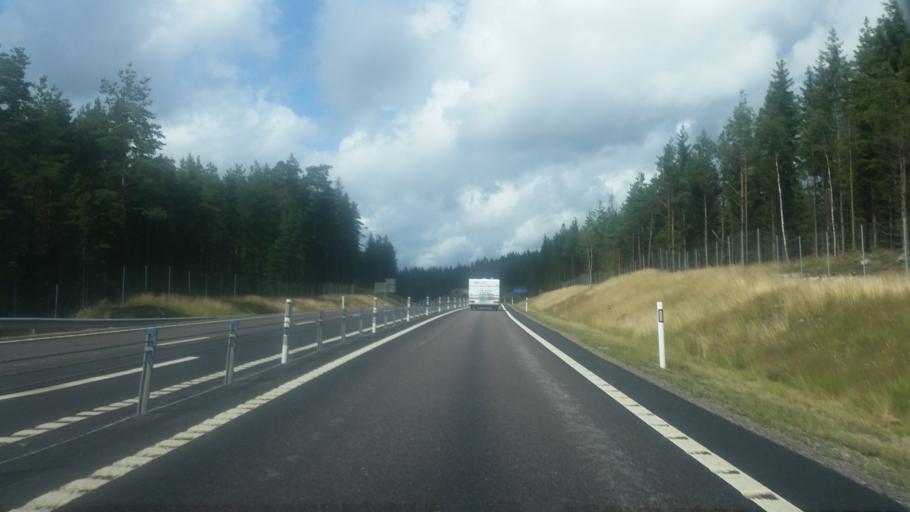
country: SE
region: Vaestra Goetaland
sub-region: Boras Kommun
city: Boras
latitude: 57.6850
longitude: 12.9299
